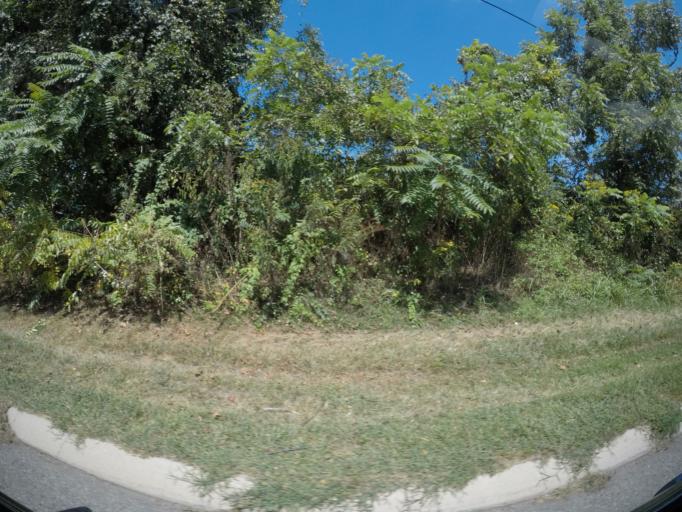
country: US
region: Maryland
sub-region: Harford County
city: South Bel Air
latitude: 39.5784
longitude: -76.3093
